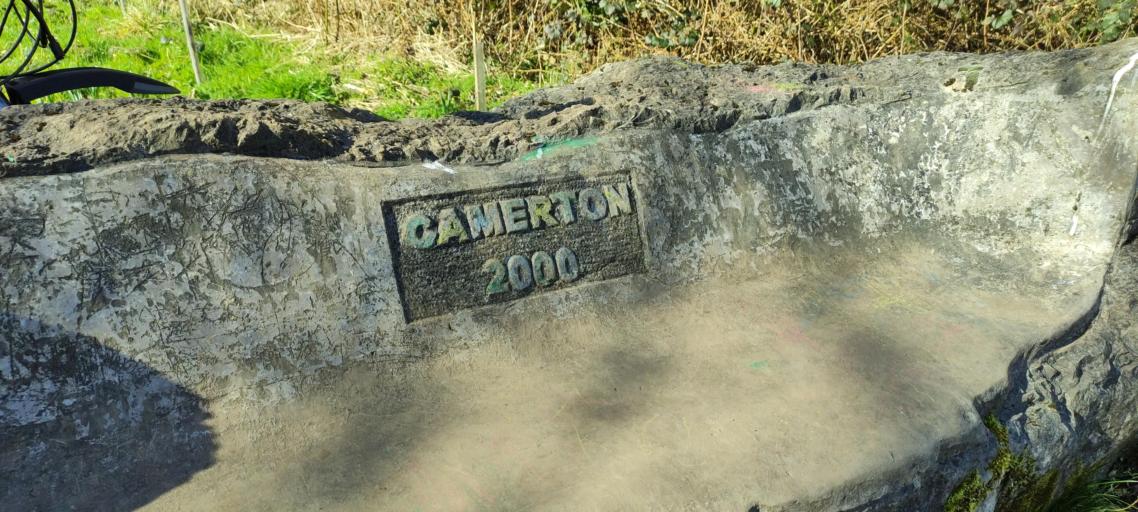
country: GB
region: England
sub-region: Cumbria
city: Flimby
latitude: 54.6638
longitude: -3.4899
